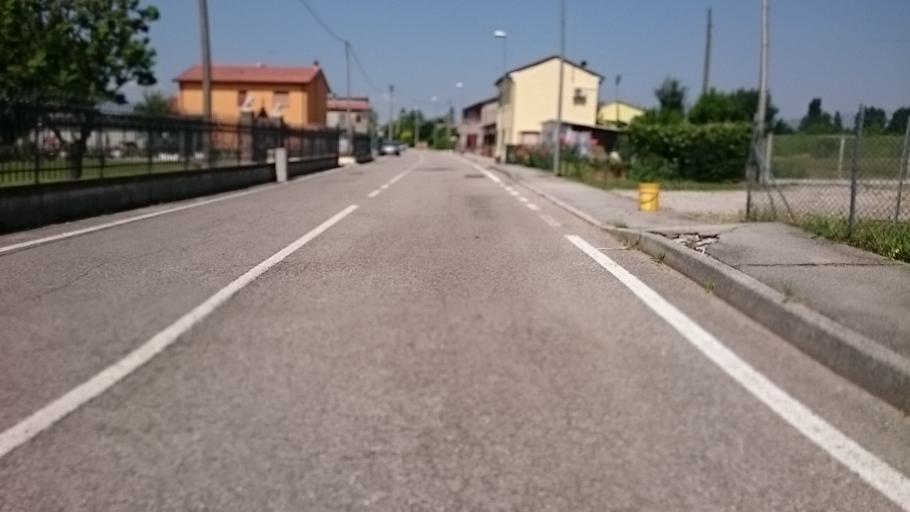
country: IT
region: Veneto
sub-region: Provincia di Padova
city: Albignasego
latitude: 45.3468
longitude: 11.8875
